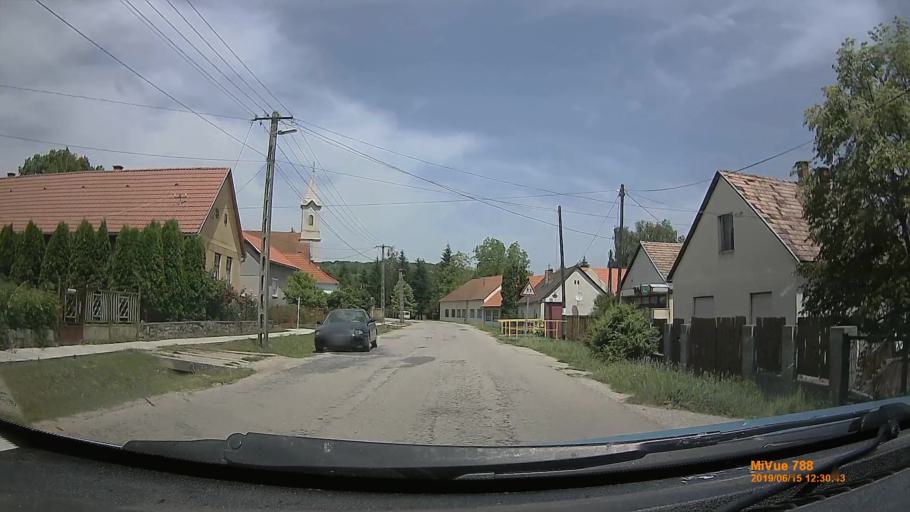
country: HU
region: Baranya
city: Buekkoesd
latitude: 46.1308
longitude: 18.0439
